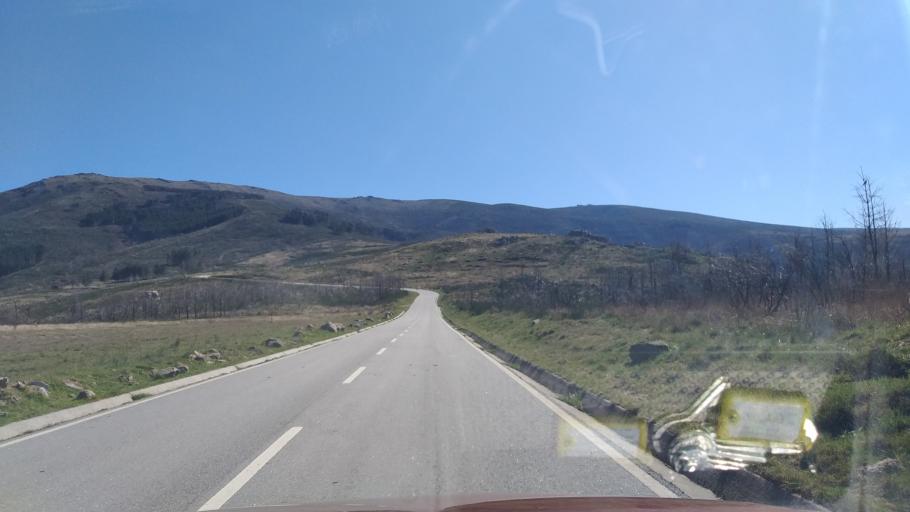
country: PT
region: Guarda
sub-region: Manteigas
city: Manteigas
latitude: 40.4901
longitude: -7.5671
